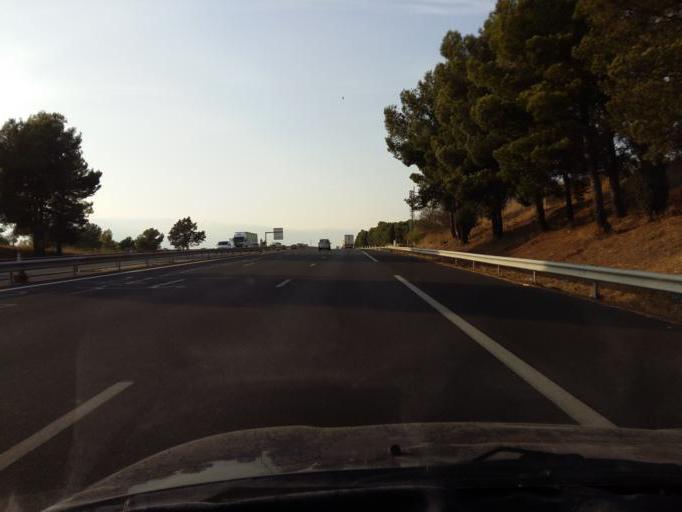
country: FR
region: Provence-Alpes-Cote d'Azur
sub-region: Departement des Bouches-du-Rhone
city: Aix-en-Provence
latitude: 43.5259
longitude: 5.4043
